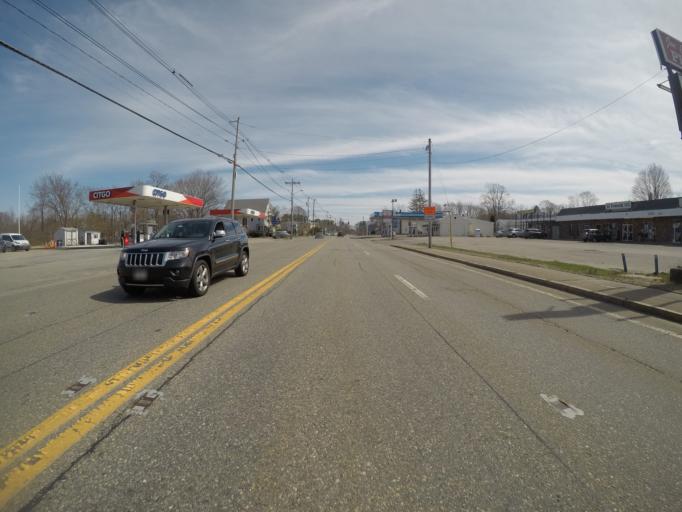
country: US
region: Massachusetts
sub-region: Bristol County
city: Easton
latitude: 42.0433
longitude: -71.0782
